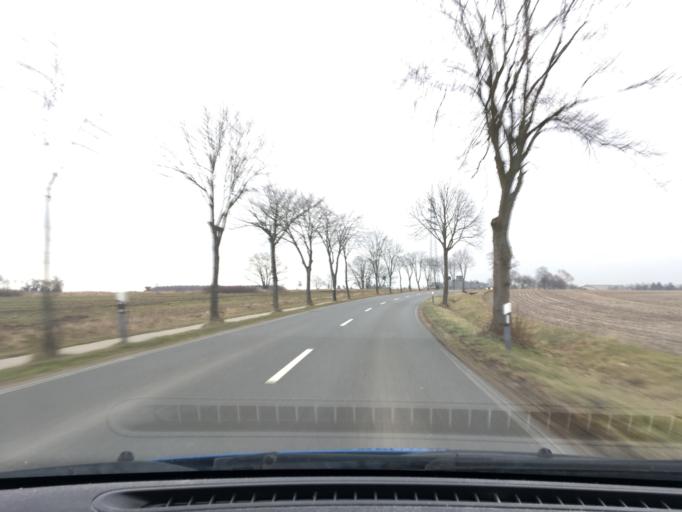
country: DE
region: Lower Saxony
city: Reppenstedt
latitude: 53.2639
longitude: 10.3778
